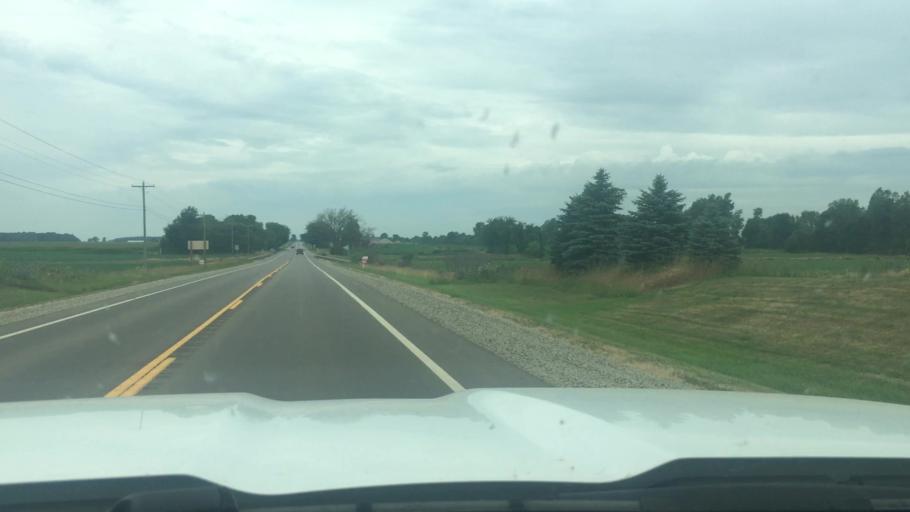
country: US
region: Michigan
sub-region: Clinton County
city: Fowler
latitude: 43.0017
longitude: -84.6812
